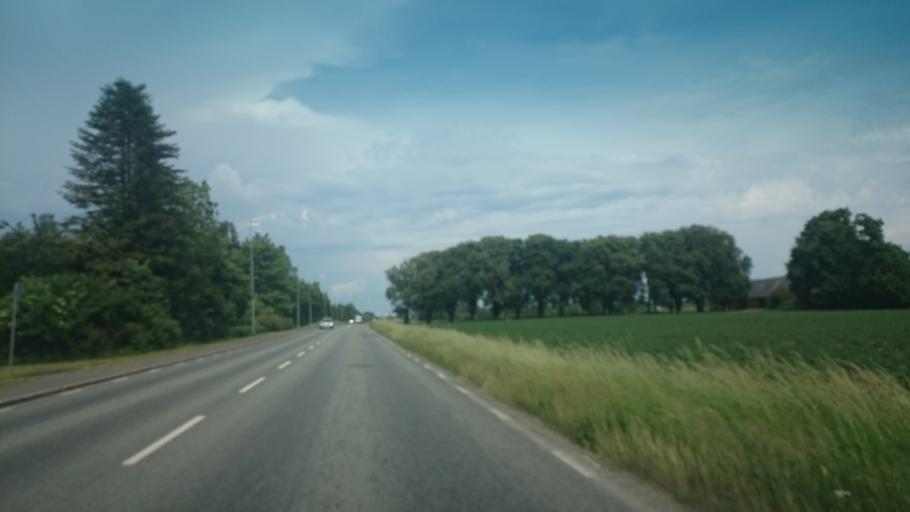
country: SE
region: Skane
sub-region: Kristianstads Kommun
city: Norra Asum
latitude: 56.0007
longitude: 14.1509
